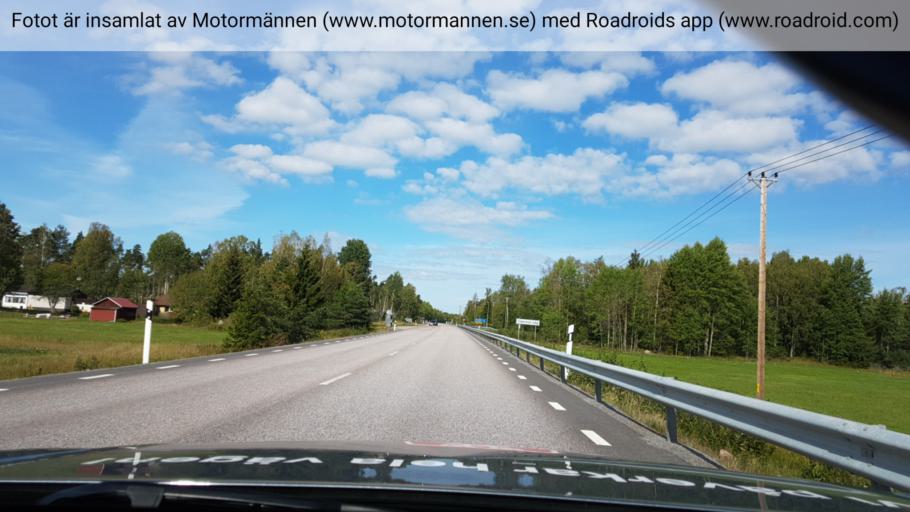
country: SE
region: Uppsala
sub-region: Osthammars Kommun
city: Bjorklinge
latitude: 59.9688
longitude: 17.3746
